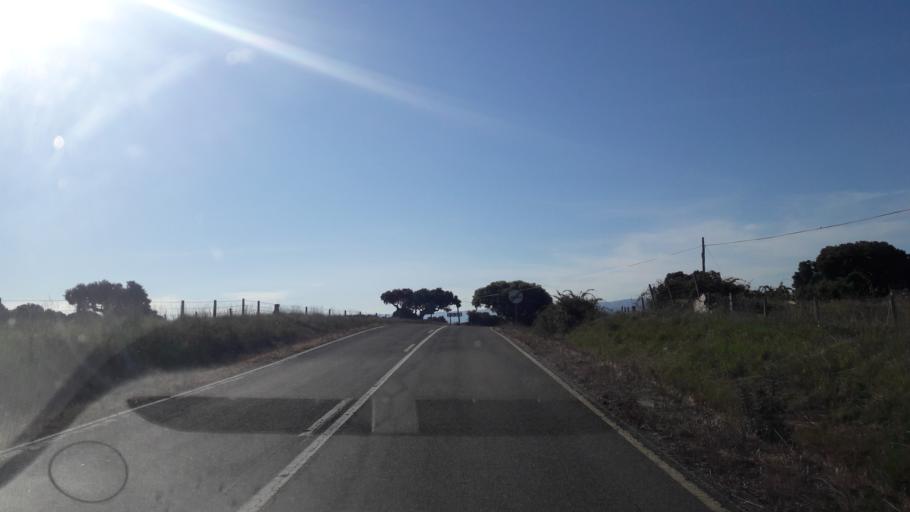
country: ES
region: Castille and Leon
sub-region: Provincia de Salamanca
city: Puente del Congosto
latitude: 40.5340
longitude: -5.5268
